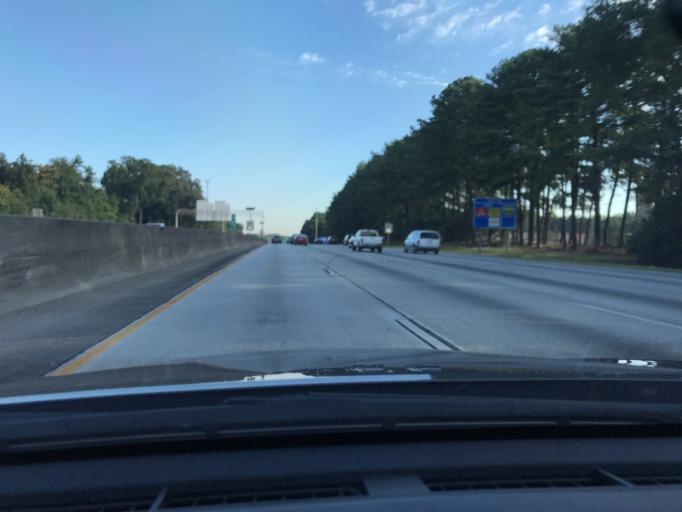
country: US
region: Georgia
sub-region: DeKalb County
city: Belvedere Park
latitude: 33.7448
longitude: -84.2306
